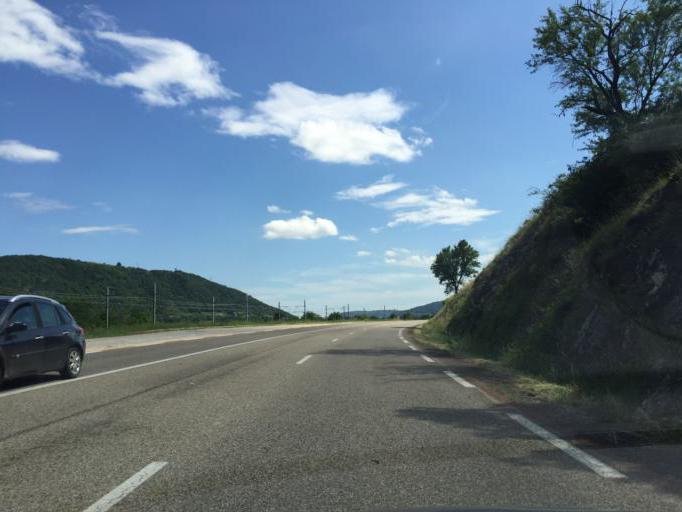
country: FR
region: Rhone-Alpes
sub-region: Departement de la Drome
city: Saint-Vallier
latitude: 45.1551
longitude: 4.8150
